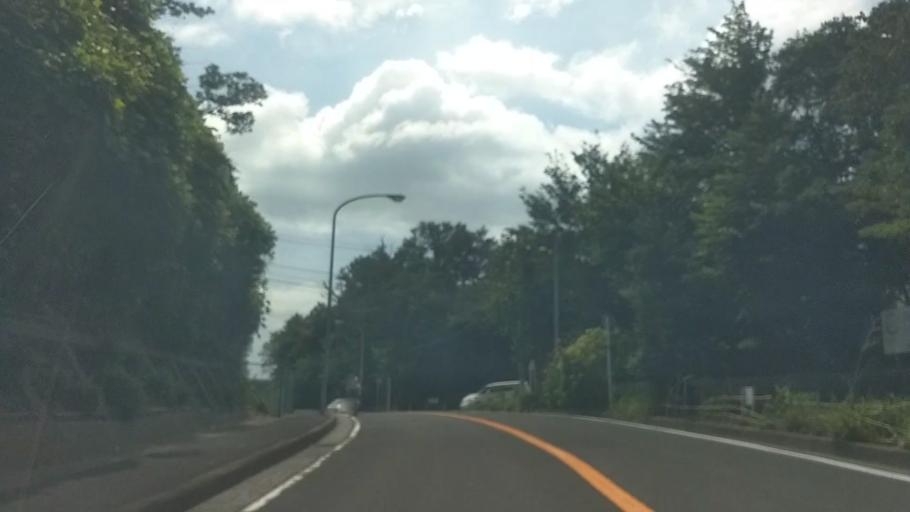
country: JP
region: Kanagawa
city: Yokosuka
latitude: 35.3603
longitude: 139.6310
